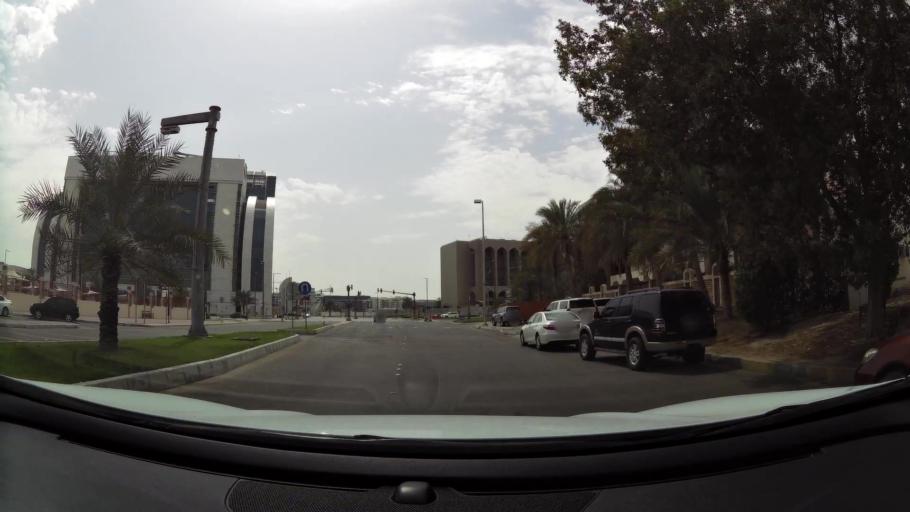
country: AE
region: Abu Dhabi
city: Abu Dhabi
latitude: 24.4580
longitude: 54.3389
